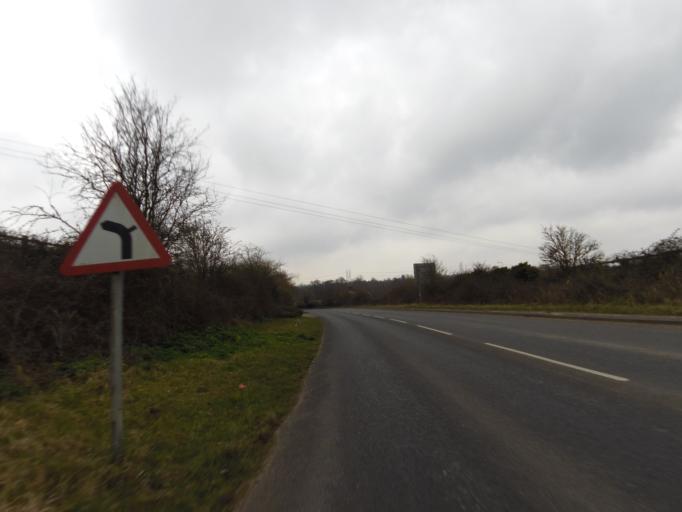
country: GB
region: England
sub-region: Suffolk
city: Wickham Market
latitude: 52.1593
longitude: 1.3811
